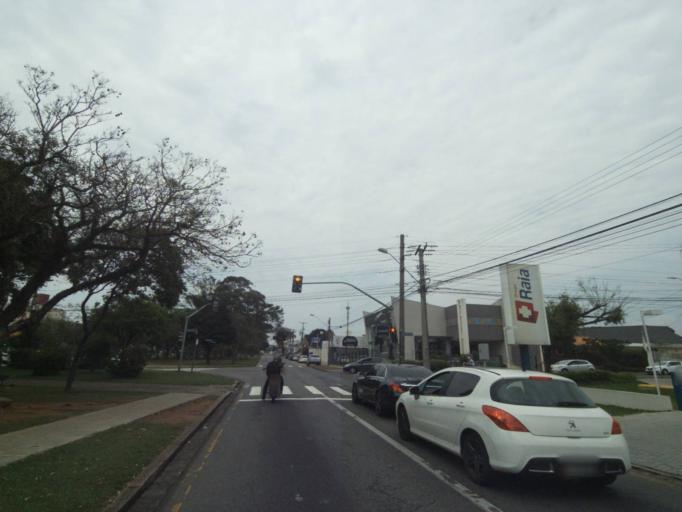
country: BR
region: Parana
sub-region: Curitiba
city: Curitiba
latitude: -25.4596
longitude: -49.3024
